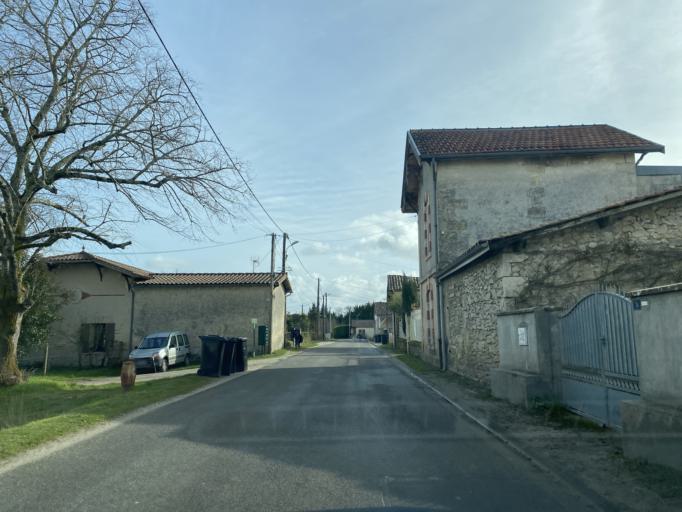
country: FR
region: Aquitaine
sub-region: Departement de la Gironde
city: Moulis-en-Medoc
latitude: 45.0570
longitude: -0.7710
